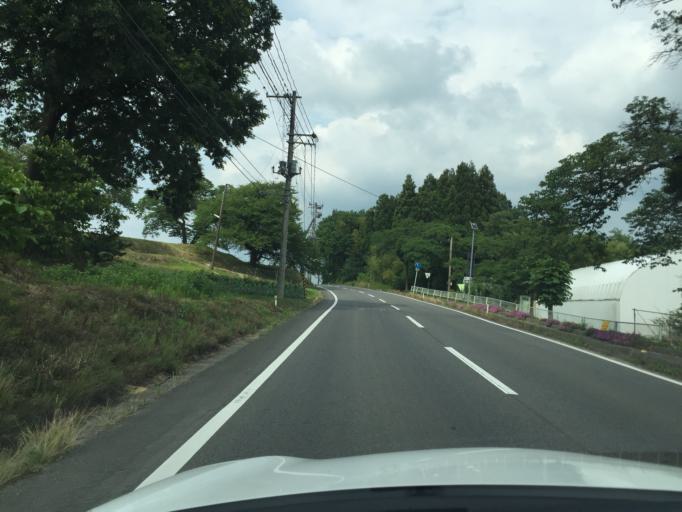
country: JP
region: Fukushima
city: Sukagawa
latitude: 37.2767
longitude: 140.4216
